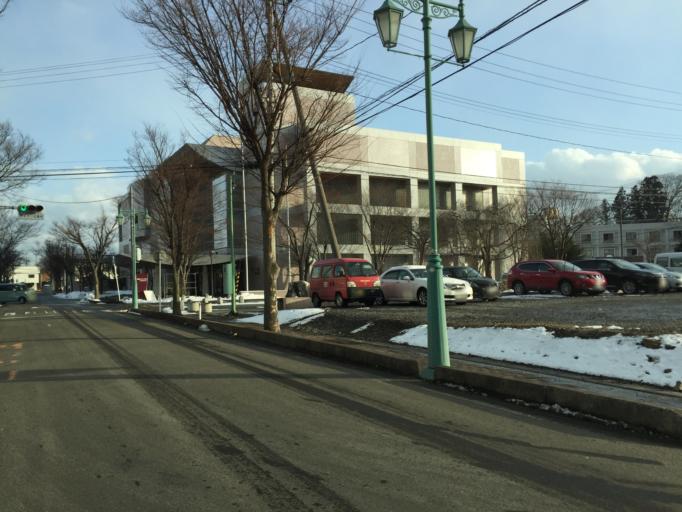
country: JP
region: Fukushima
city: Fukushima-shi
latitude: 37.8323
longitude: 140.4480
